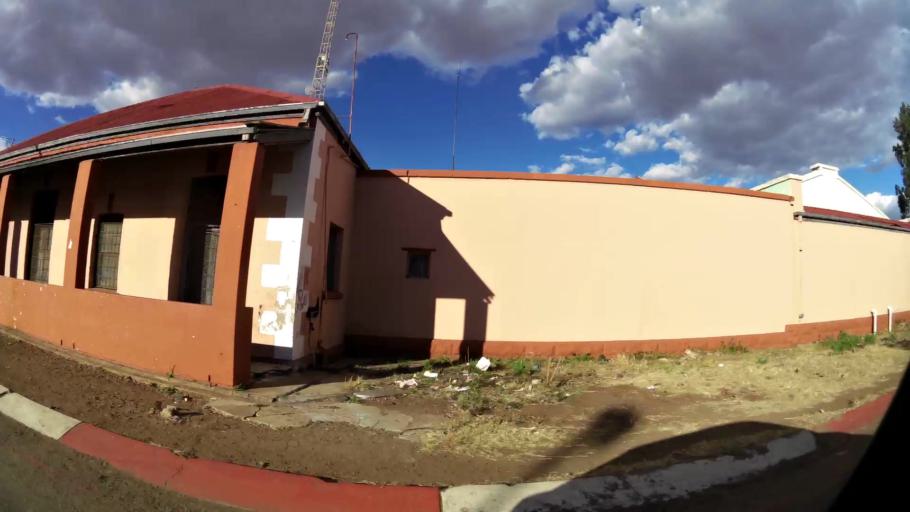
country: ZA
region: North-West
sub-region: Dr Kenneth Kaunda District Municipality
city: Potchefstroom
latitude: -26.7157
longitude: 27.0832
